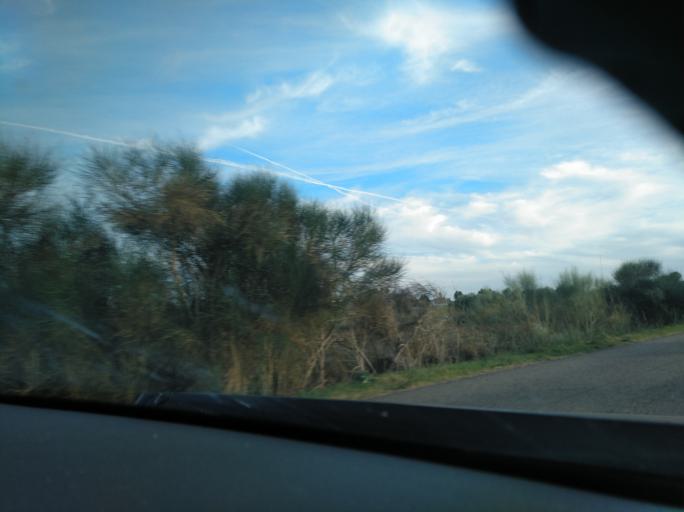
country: PT
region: Evora
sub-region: Arraiolos
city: Arraiolos
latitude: 38.8334
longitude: -7.8339
